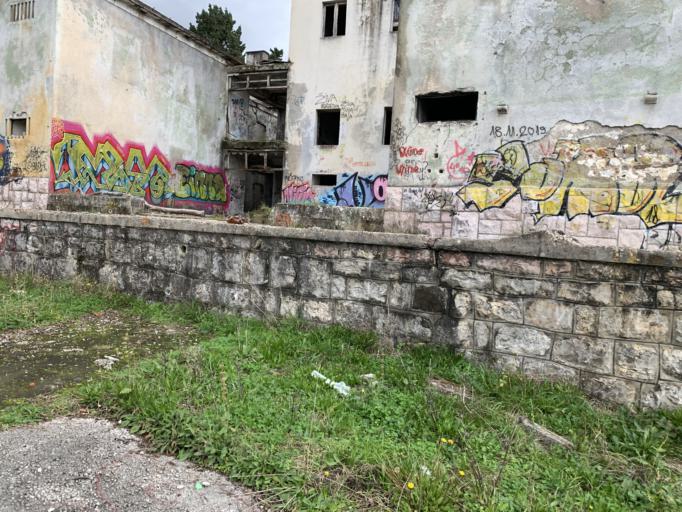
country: ME
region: Tivat
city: Tivat
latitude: 42.4230
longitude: 18.7039
